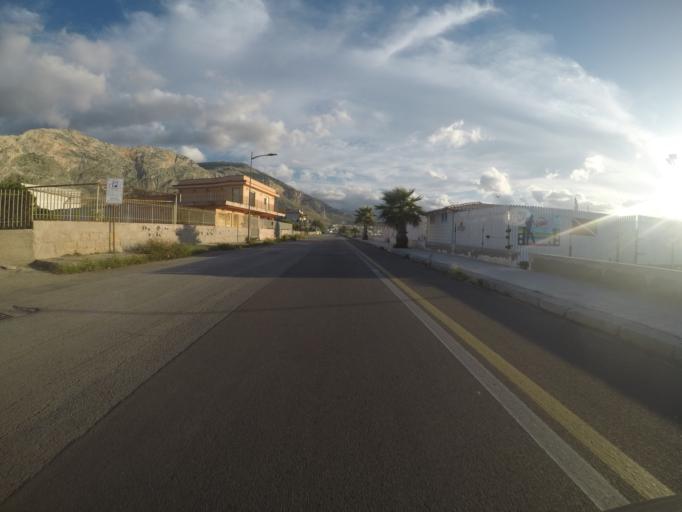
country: IT
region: Sicily
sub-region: Palermo
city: Isola delle Femmine
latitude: 38.1974
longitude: 13.2437
